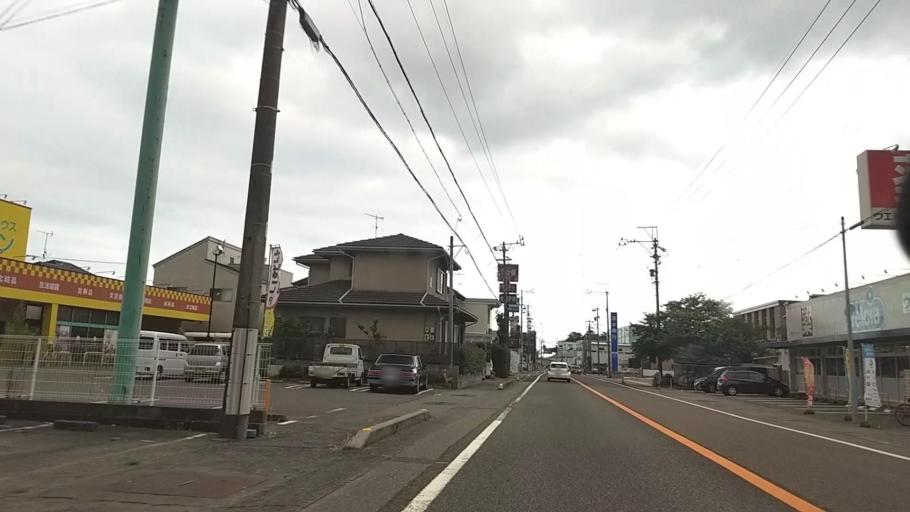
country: JP
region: Shizuoka
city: Shizuoka-shi
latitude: 35.0601
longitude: 138.5255
